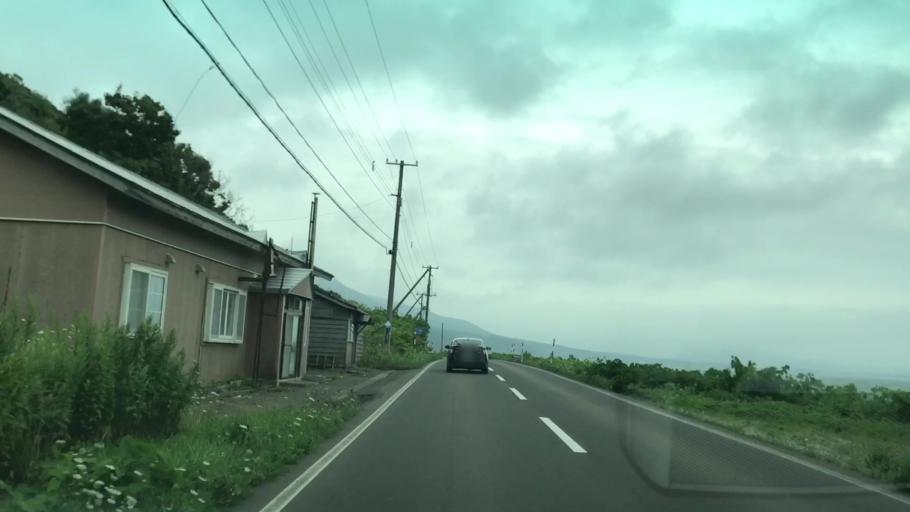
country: JP
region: Hokkaido
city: Iwanai
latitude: 42.8085
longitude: 140.3046
